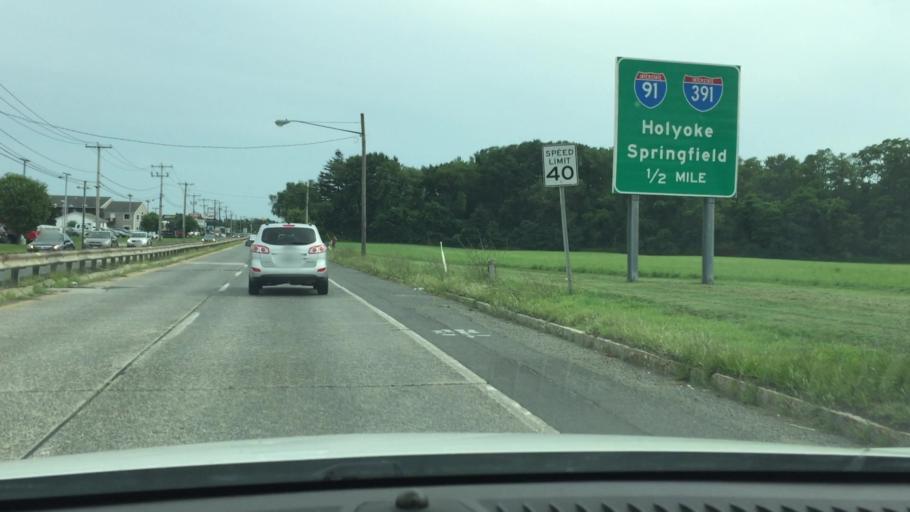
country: US
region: Massachusetts
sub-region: Hampden County
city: Chicopee
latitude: 42.1426
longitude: -72.6280
